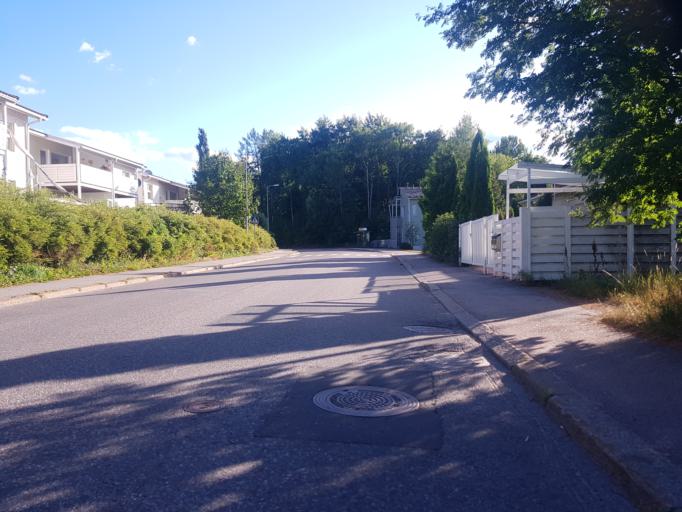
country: FI
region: Uusimaa
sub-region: Helsinki
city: Vantaa
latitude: 60.2596
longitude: 24.9813
